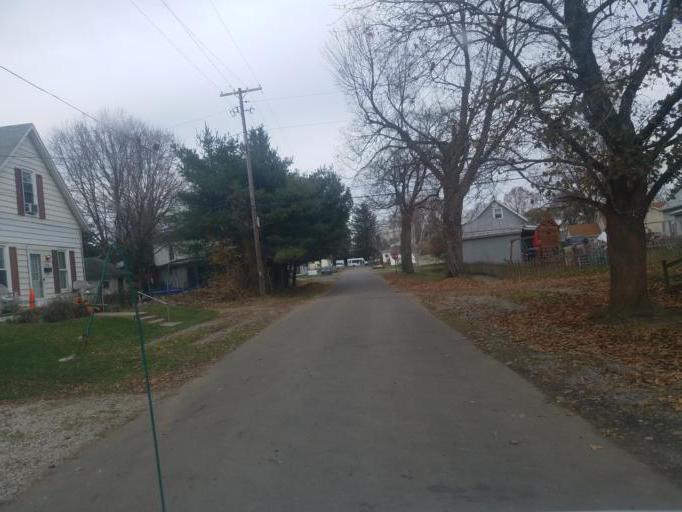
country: US
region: Ohio
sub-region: Knox County
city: Mount Vernon
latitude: 40.3881
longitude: -82.4726
